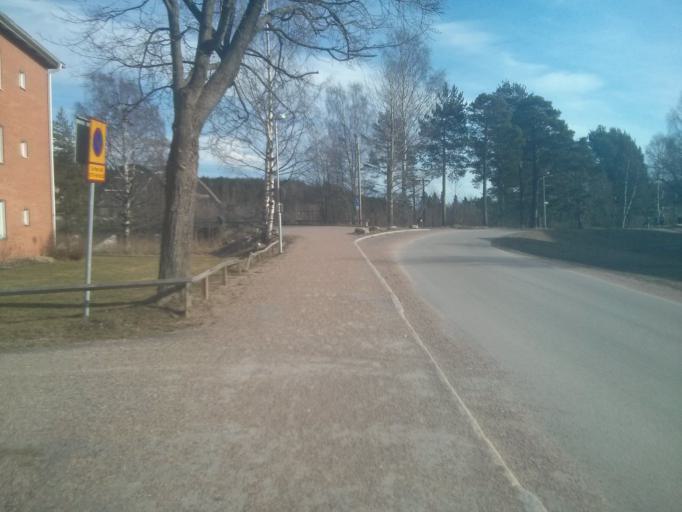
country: SE
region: Vaesternorrland
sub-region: Sundsvalls Kommun
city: Kvissleby
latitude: 62.3005
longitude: 17.3814
